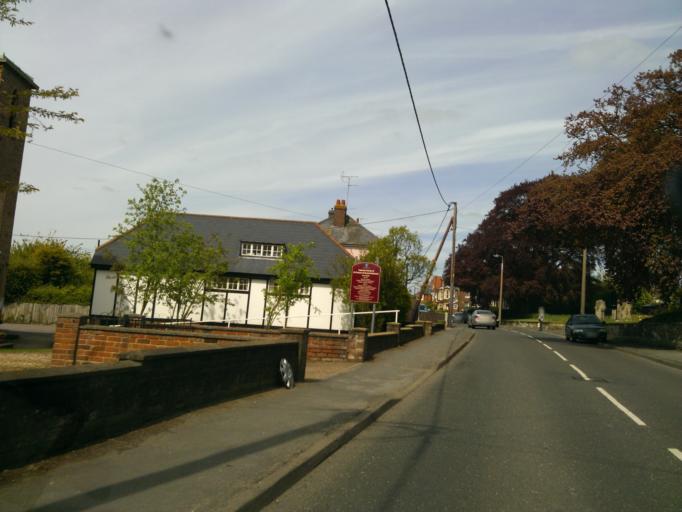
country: GB
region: England
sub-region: Essex
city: Earls Colne
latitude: 51.9435
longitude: 0.6456
